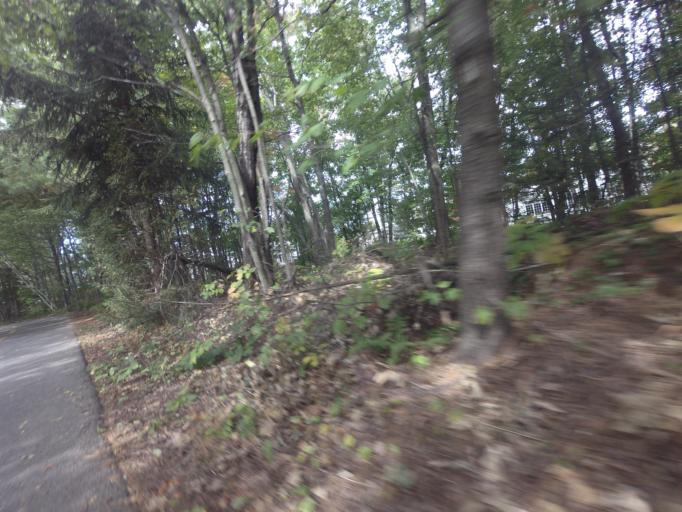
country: CA
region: Quebec
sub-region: Laurentides
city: Blainville
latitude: 45.6857
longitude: -73.8832
